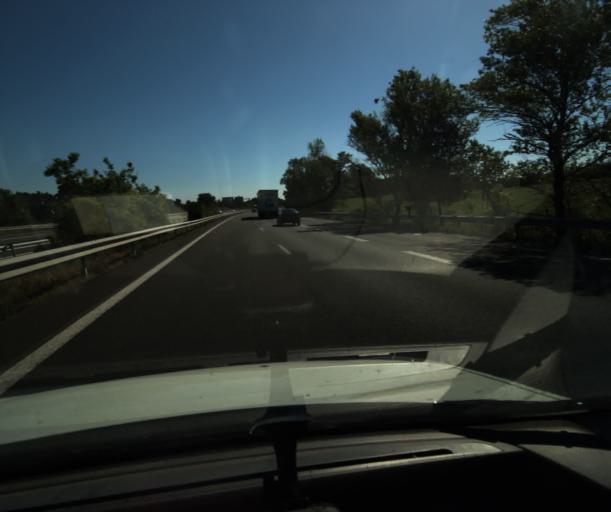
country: FR
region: Languedoc-Roussillon
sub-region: Departement de l'Aude
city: Trebes
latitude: 43.1950
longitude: 2.4209
